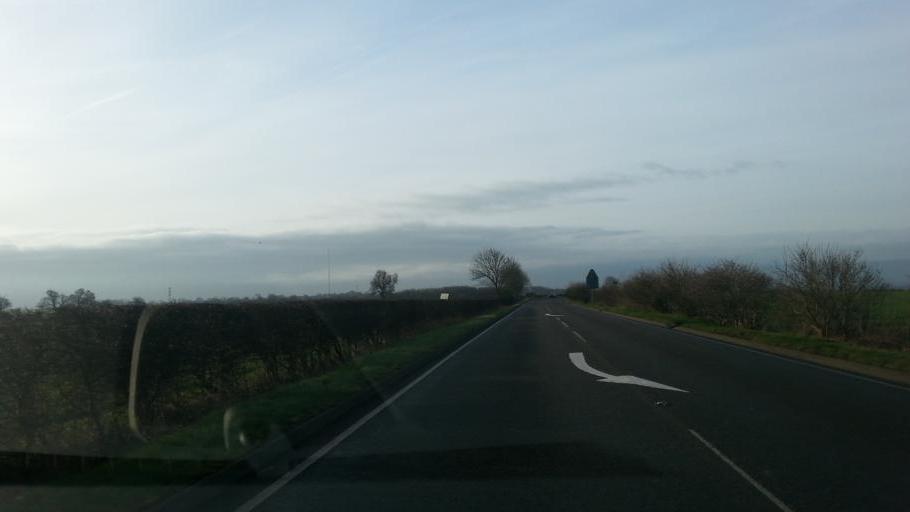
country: GB
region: England
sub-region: Leicestershire
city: Wymondham
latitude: 52.8362
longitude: -0.8032
